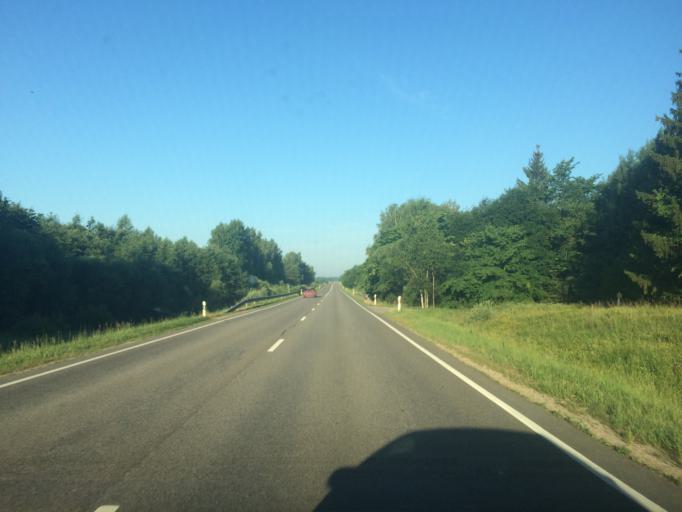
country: LT
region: Utenos apskritis
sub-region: Anyksciai
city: Anyksciai
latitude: 55.3903
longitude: 25.0642
